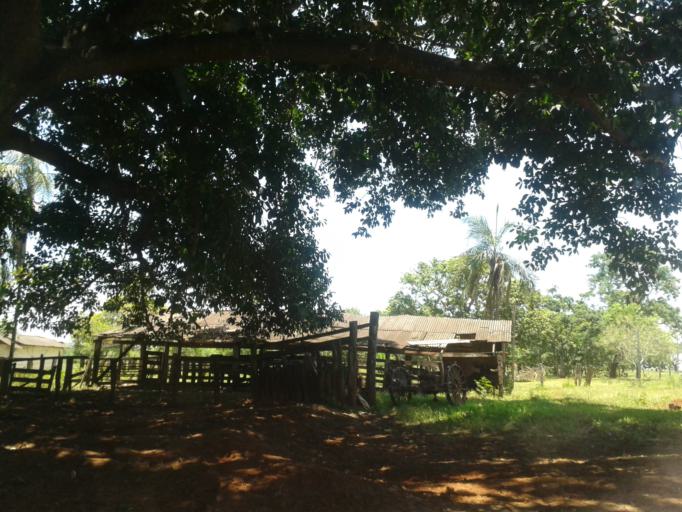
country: BR
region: Minas Gerais
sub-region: Santa Vitoria
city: Santa Vitoria
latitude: -19.2280
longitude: -50.4751
